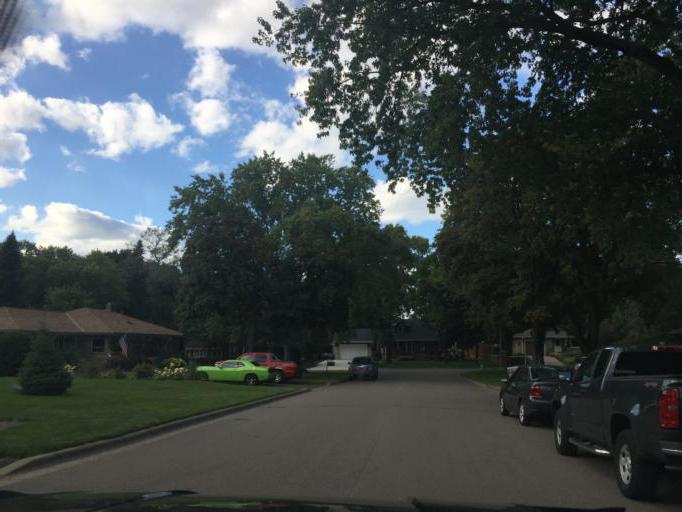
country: US
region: Minnesota
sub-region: Ramsey County
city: Roseville
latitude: 45.0085
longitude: -93.1430
